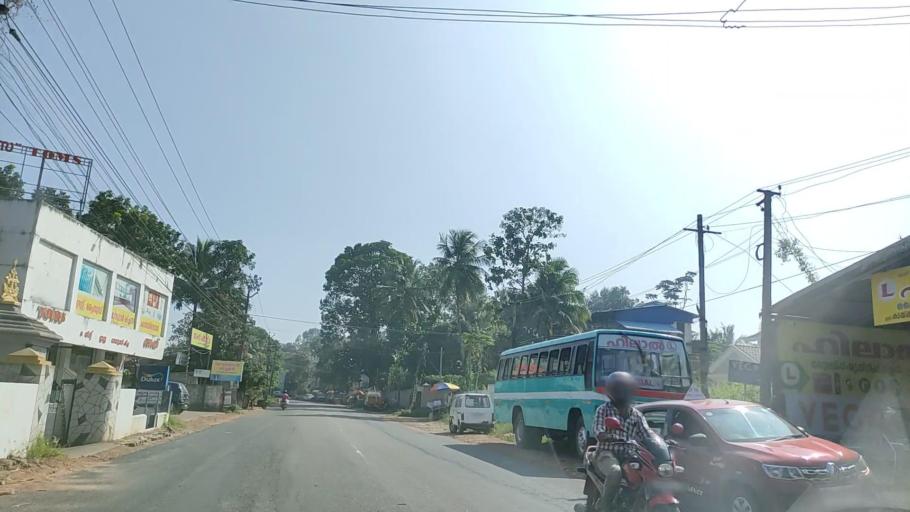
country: IN
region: Kerala
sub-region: Kollam
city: Punalur
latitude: 8.9272
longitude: 76.9227
